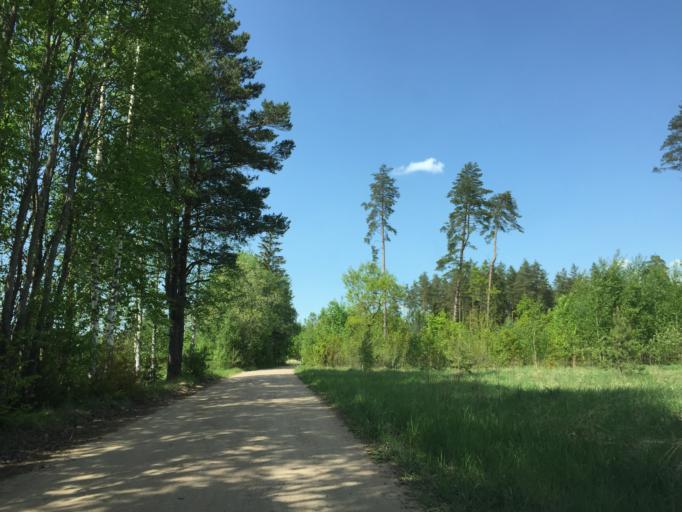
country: LV
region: Baldone
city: Baldone
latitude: 56.8027
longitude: 24.4247
